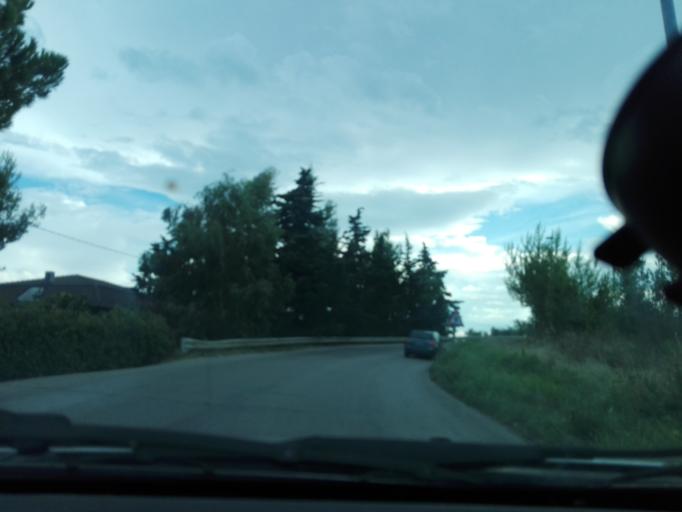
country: IT
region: Abruzzo
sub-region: Provincia di Pescara
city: Cappelle sul Tavo
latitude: 42.4581
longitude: 14.1157
